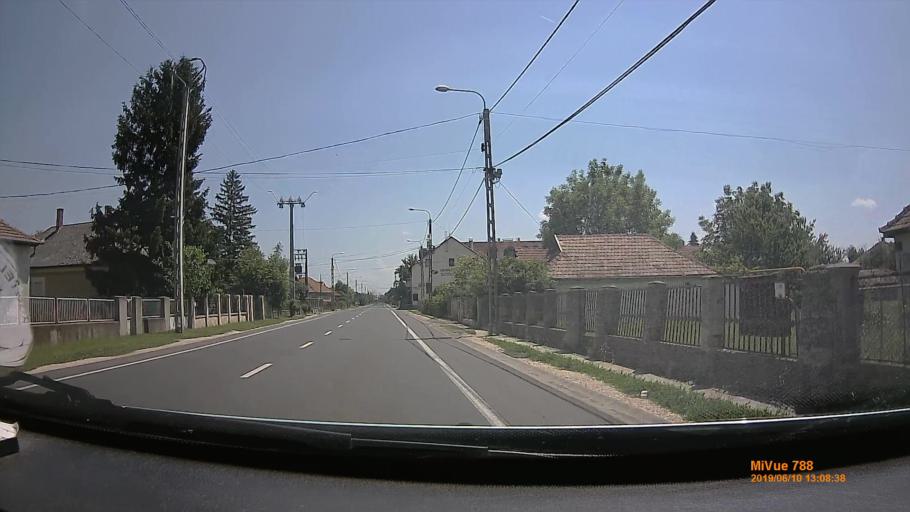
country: HU
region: Borsod-Abauj-Zemplen
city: Hernadnemeti
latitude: 48.0786
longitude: 20.9733
